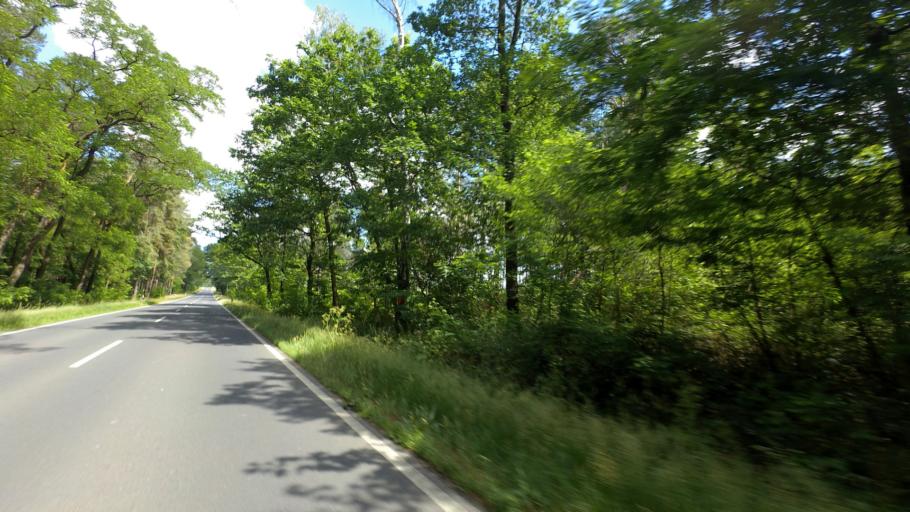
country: DE
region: Brandenburg
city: Sonnewalde
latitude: 51.7253
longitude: 13.6756
